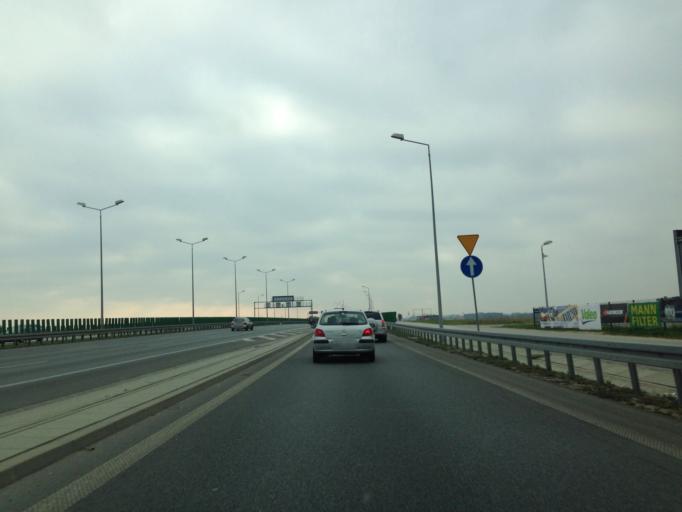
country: PL
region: Masovian Voivodeship
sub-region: Warszawa
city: Bemowo
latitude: 52.2388
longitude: 20.8872
